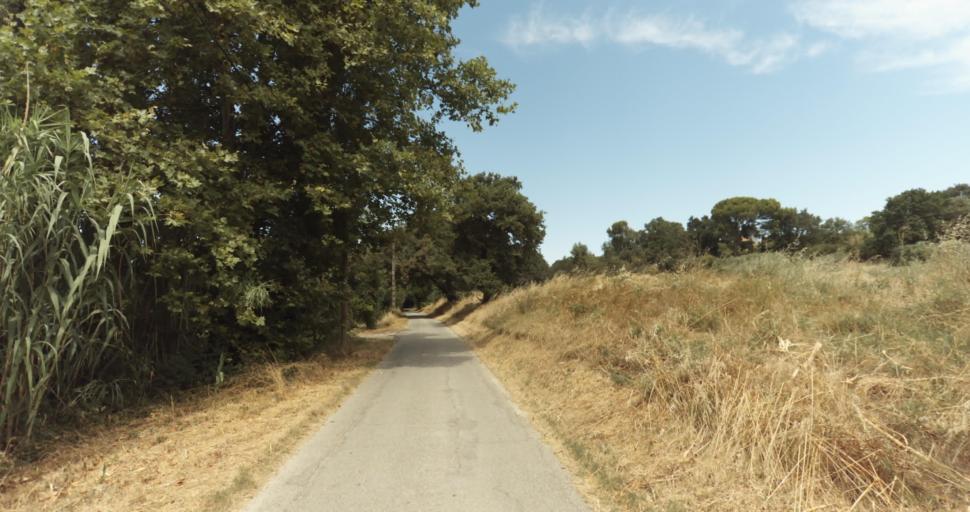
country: FR
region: Provence-Alpes-Cote d'Azur
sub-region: Departement du Vaucluse
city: Monteux
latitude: 44.0513
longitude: 4.9881
